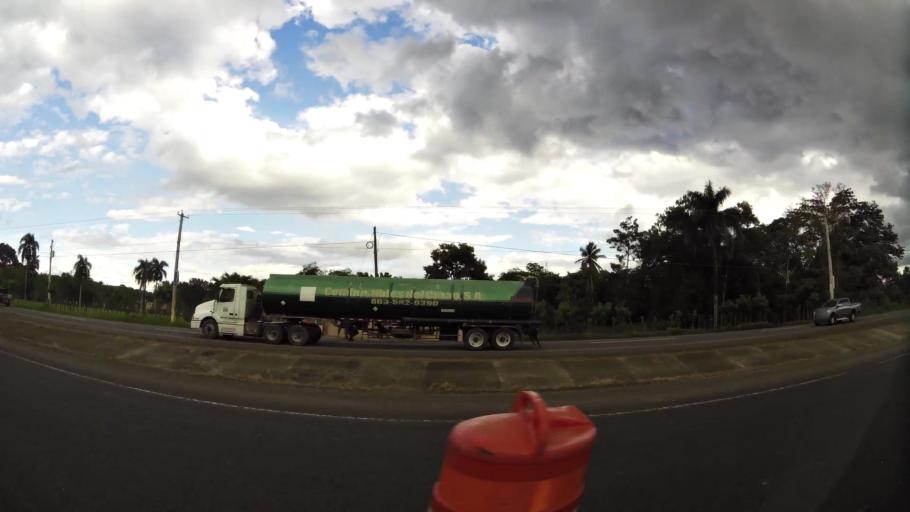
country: DO
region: Monsenor Nouel
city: Sabana del Puerto
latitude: 19.0630
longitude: -70.4461
